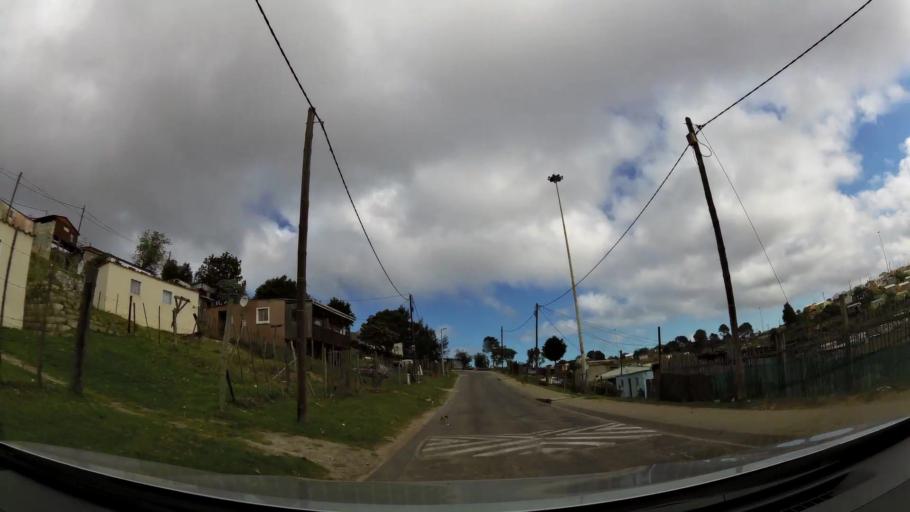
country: ZA
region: Western Cape
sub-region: Eden District Municipality
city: Knysna
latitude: -34.0336
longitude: 23.1043
